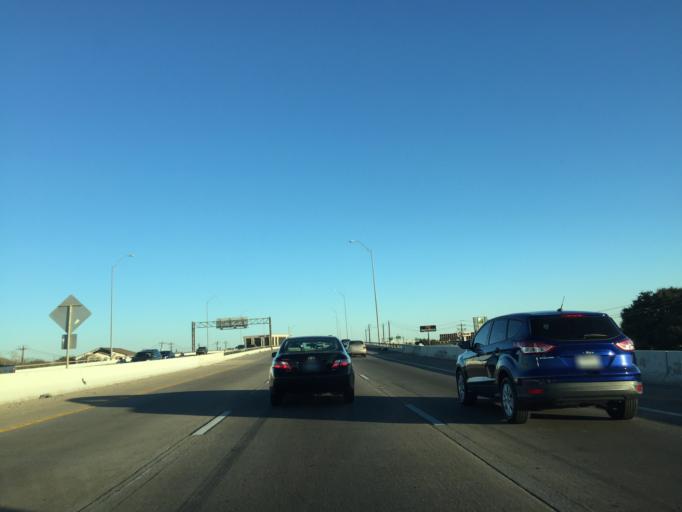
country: US
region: Texas
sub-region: Travis County
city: Austin
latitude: 30.3452
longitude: -97.7076
